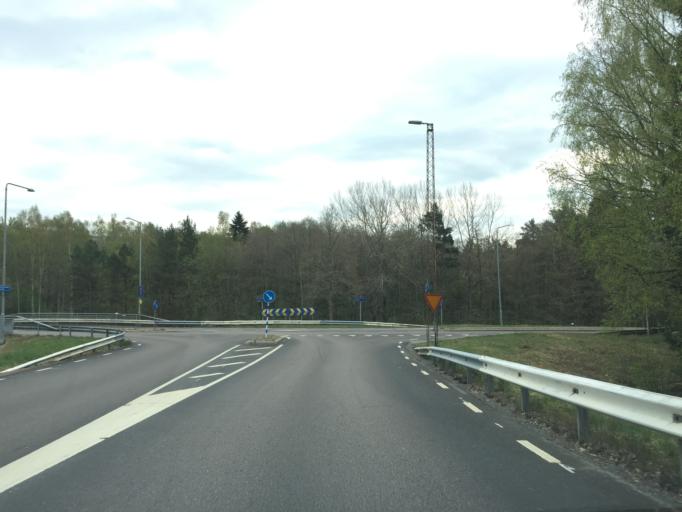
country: SE
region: Vaestra Goetaland
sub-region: Goteborg
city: Rannebergen
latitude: 57.8045
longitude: 12.0621
